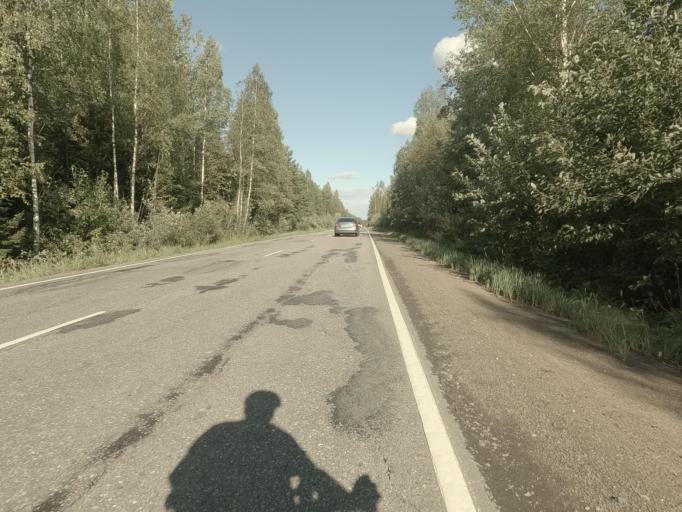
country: RU
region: Leningrad
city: Borisova Griva
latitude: 59.9852
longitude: 30.9033
